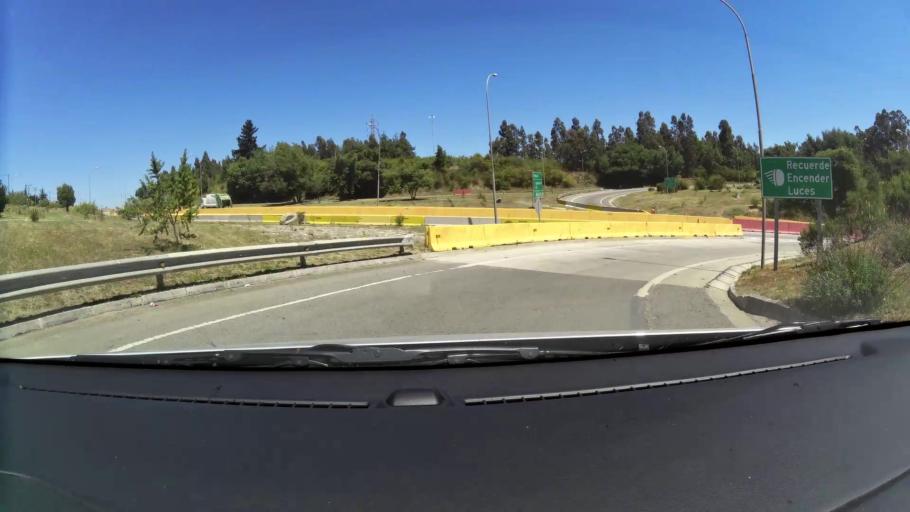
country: CL
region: Valparaiso
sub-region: Provincia de Valparaiso
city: Valparaiso
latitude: -33.0661
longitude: -71.6366
